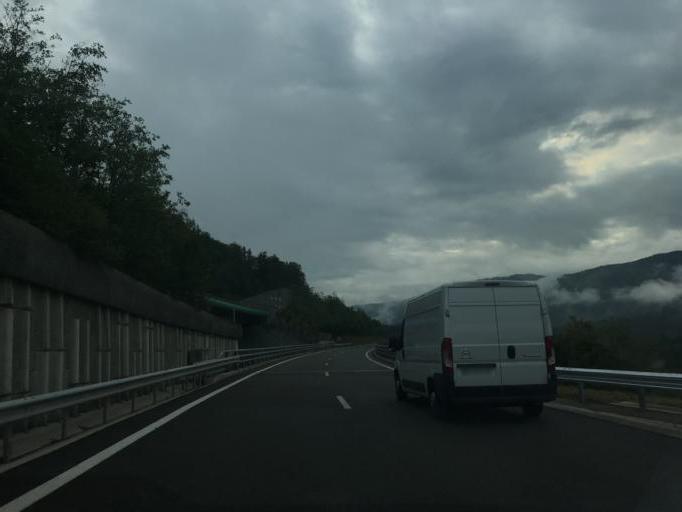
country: FR
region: Rhone-Alpes
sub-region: Departement de l'Ain
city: Montreal-la-Cluse
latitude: 46.1935
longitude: 5.5785
